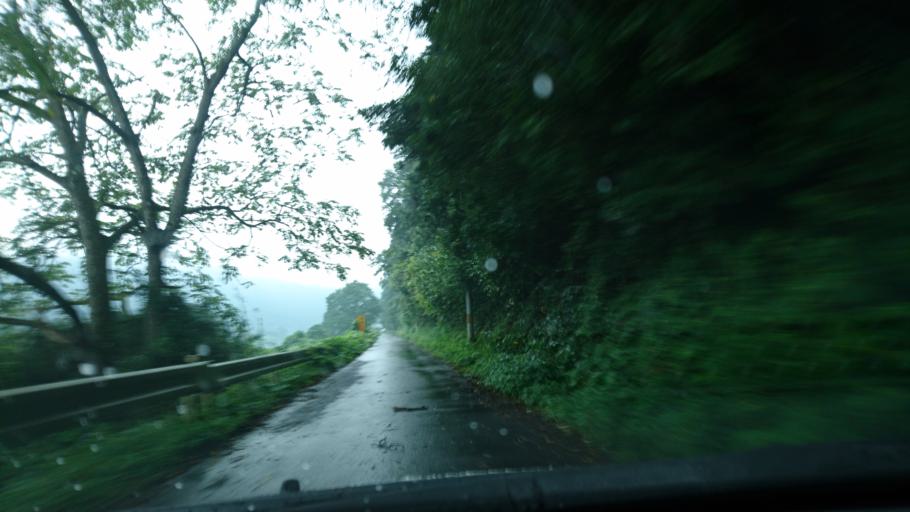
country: JP
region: Iwate
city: Ichinoseki
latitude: 38.8756
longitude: 141.2594
